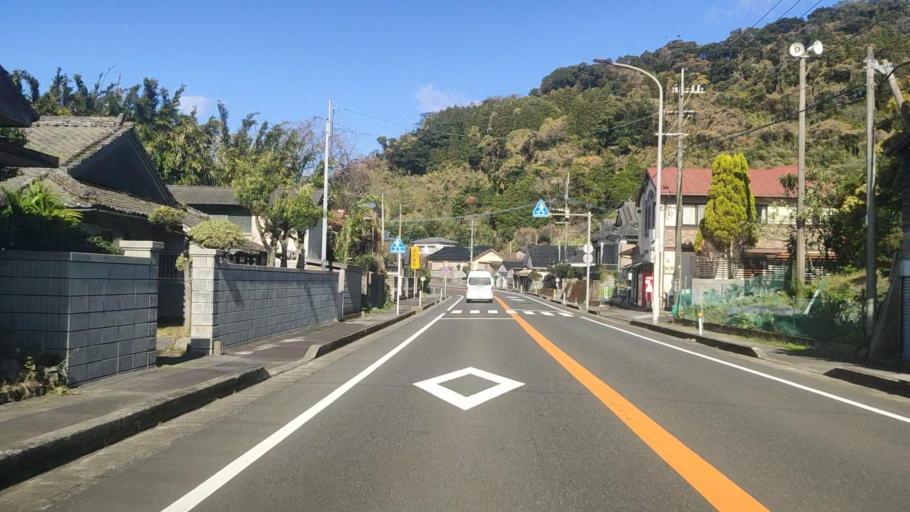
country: JP
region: Kagoshima
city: Hamanoichi
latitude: 31.5999
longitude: 130.7880
